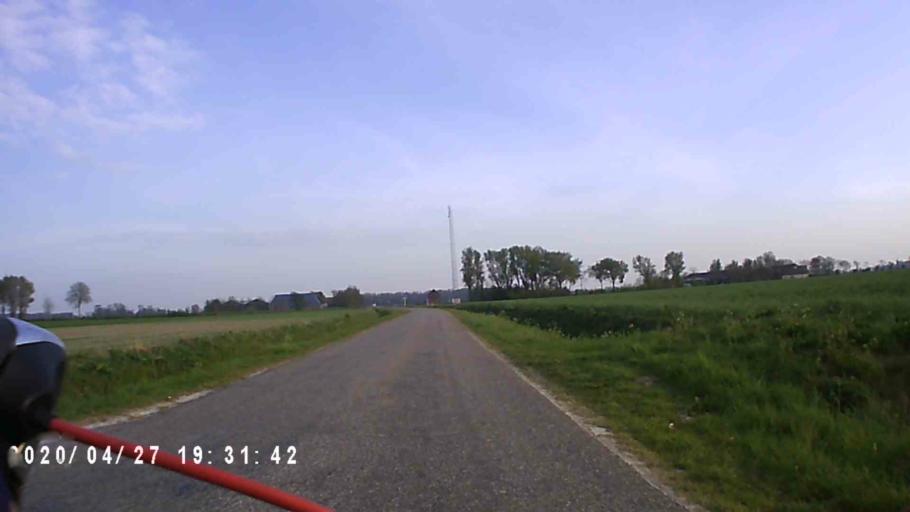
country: NL
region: Groningen
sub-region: Gemeente Winsum
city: Winsum
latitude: 53.3825
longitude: 6.4579
